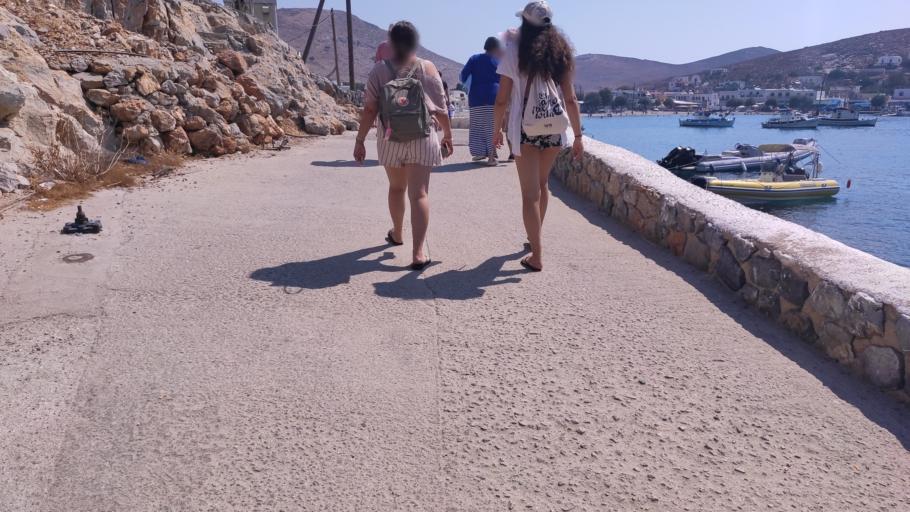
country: GR
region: South Aegean
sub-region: Nomos Dodekanisou
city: Pylion
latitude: 36.9324
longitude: 27.1309
